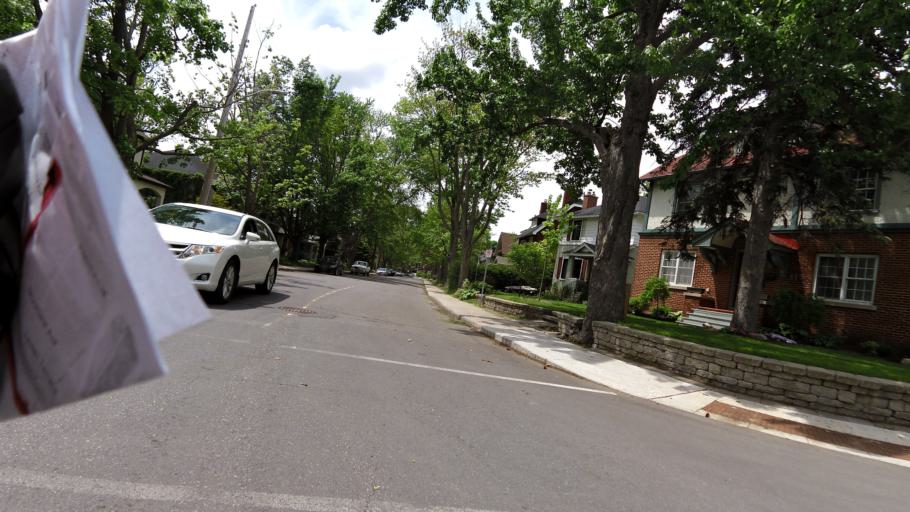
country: CA
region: Ontario
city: Ottawa
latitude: 45.3953
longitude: -75.6931
